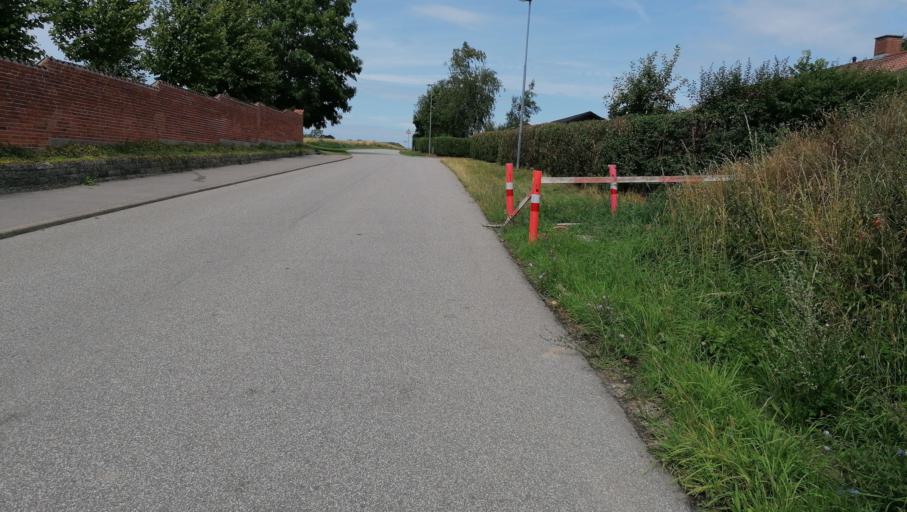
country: DK
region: Zealand
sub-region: Odsherred Kommune
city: Horve
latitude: 55.7585
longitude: 11.4555
